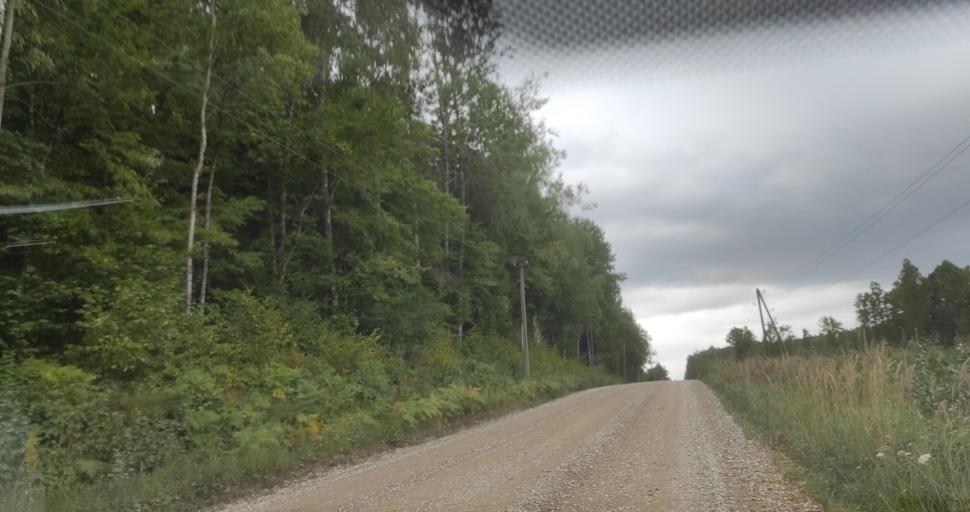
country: LV
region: Durbe
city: Liegi
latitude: 56.6920
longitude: 21.3969
